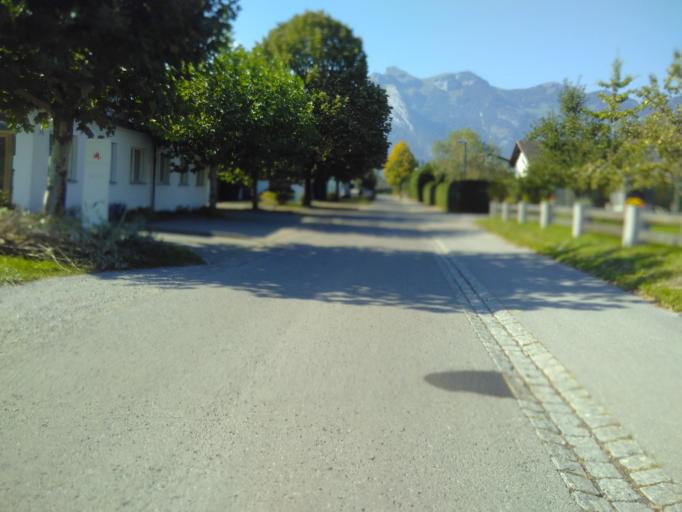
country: AT
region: Vorarlberg
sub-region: Politischer Bezirk Feldkirch
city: Nofels
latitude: 47.2599
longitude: 9.5663
